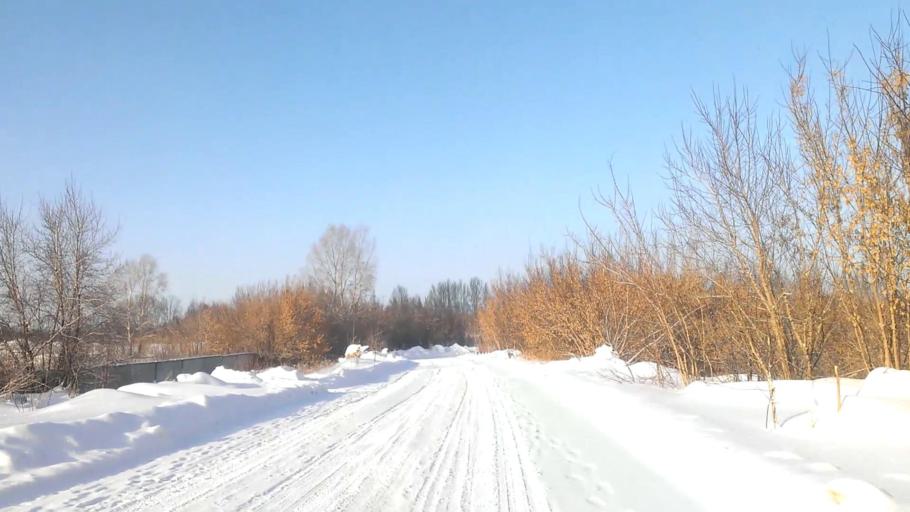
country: RU
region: Altai Krai
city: Novosilikatnyy
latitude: 53.3453
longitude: 83.6298
